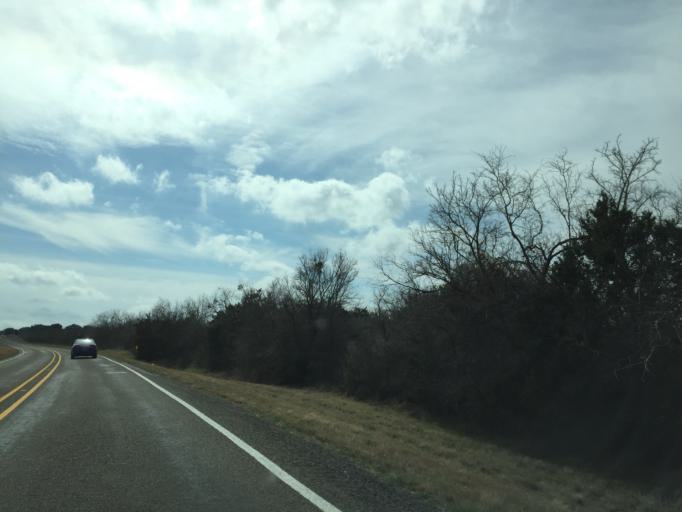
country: US
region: Texas
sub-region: Burnet County
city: Granite Shoals
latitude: 30.5057
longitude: -98.4411
